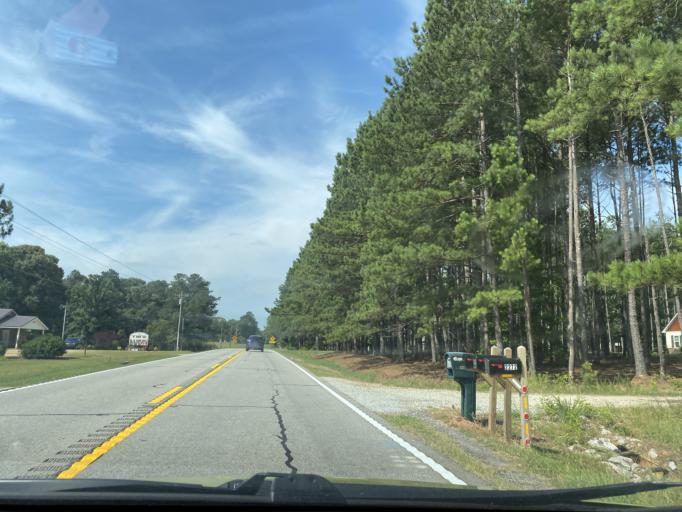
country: US
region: Georgia
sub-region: Coweta County
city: East Newnan
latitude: 33.2639
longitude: -84.7199
